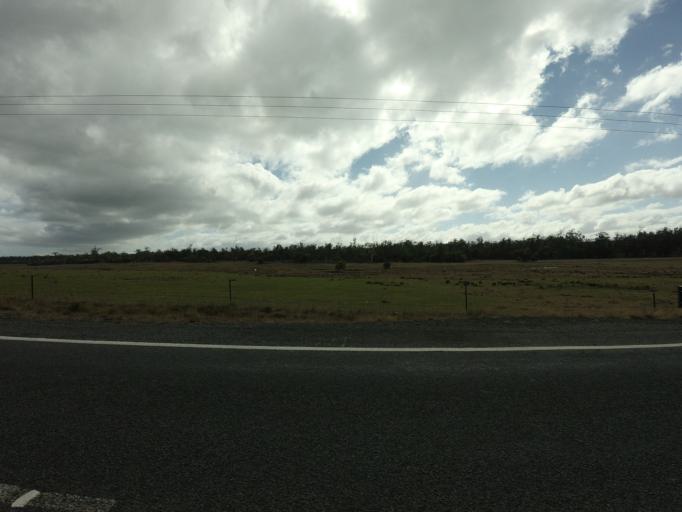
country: AU
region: Tasmania
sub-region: Northern Midlands
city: Evandale
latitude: -41.8305
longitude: 147.4895
